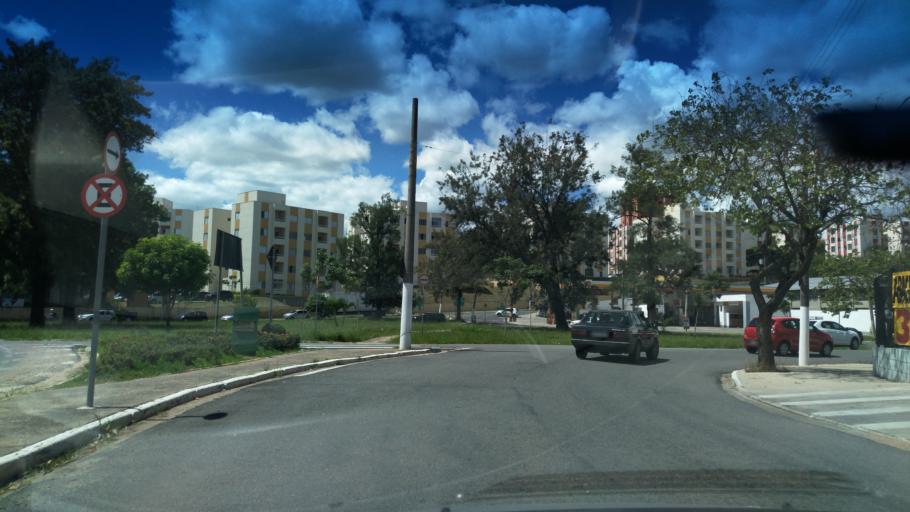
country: BR
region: Sao Paulo
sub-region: Valinhos
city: Valinhos
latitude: -22.9771
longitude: -46.9889
